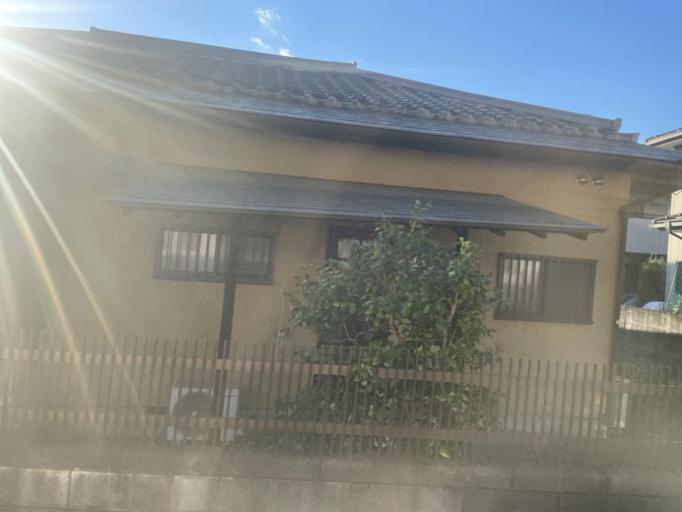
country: JP
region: Saitama
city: Chichibu
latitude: 35.9778
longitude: 139.0752
